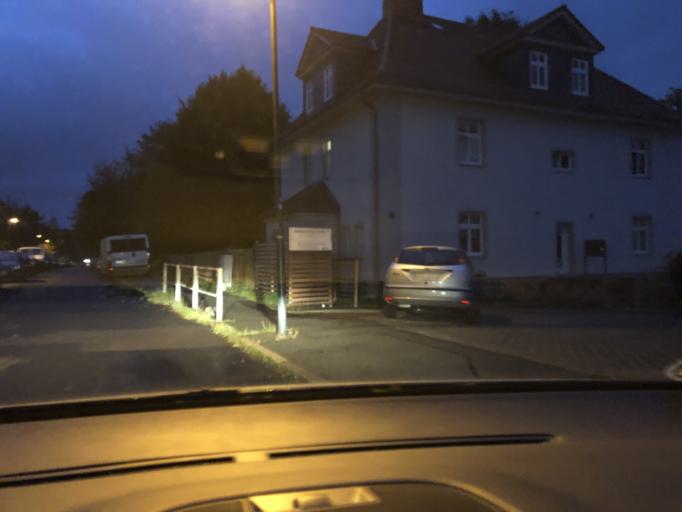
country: DE
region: Thuringia
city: Arnstadt
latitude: 50.8417
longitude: 10.9443
